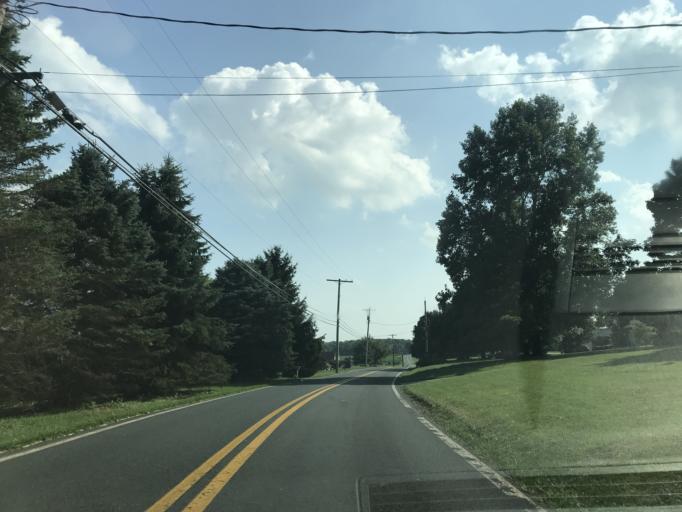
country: US
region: Maryland
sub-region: Carroll County
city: Westminster
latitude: 39.6133
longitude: -76.9822
